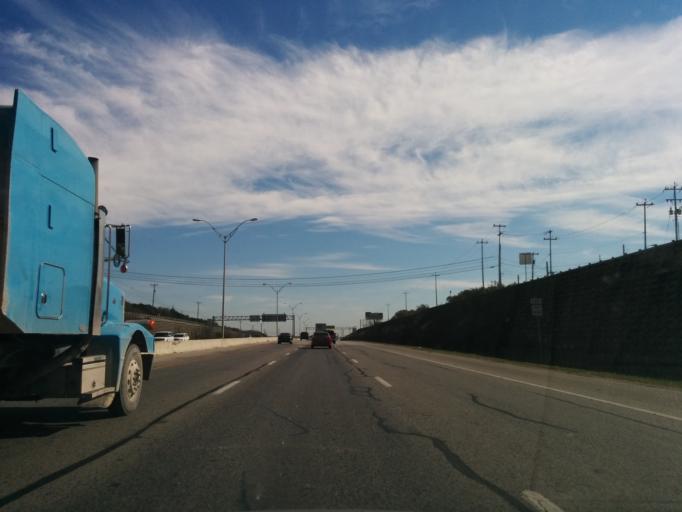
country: US
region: Texas
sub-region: Bexar County
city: Shavano Park
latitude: 29.5922
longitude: -98.5865
